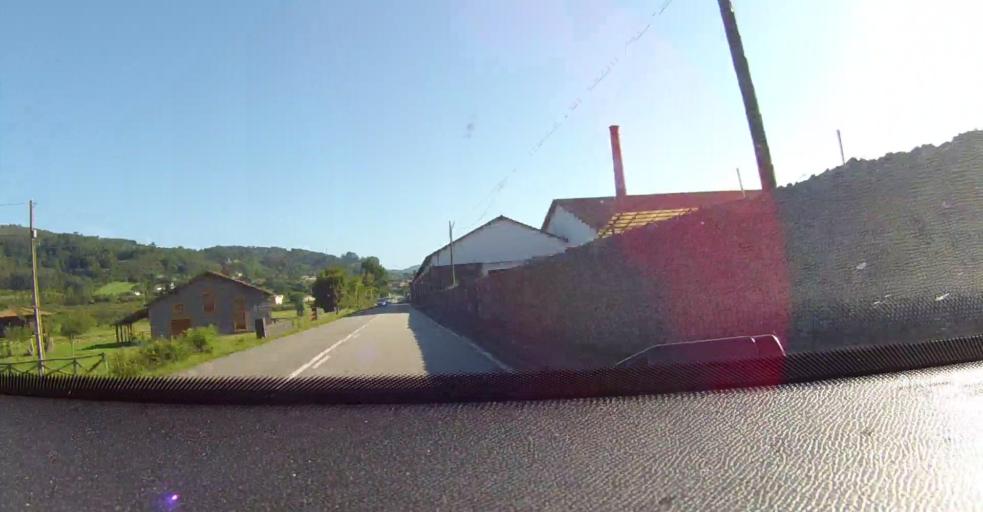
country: ES
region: Asturias
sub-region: Province of Asturias
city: Villaviciosa
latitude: 43.4962
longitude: -5.4225
